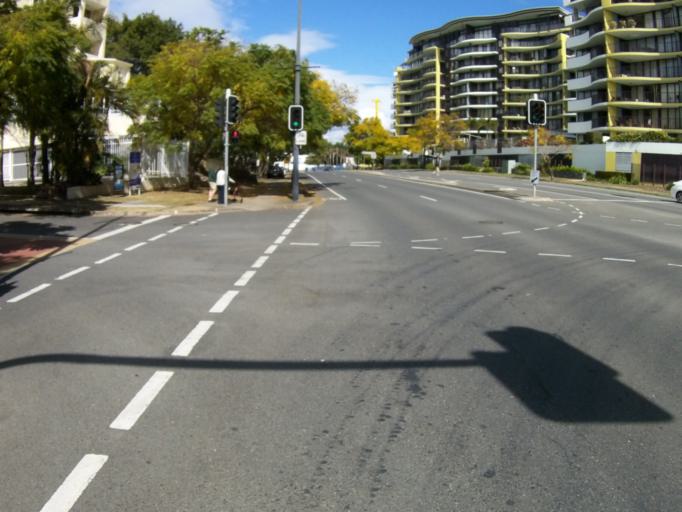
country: AU
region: Queensland
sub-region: Brisbane
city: Toowong
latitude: -27.4800
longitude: 152.9970
